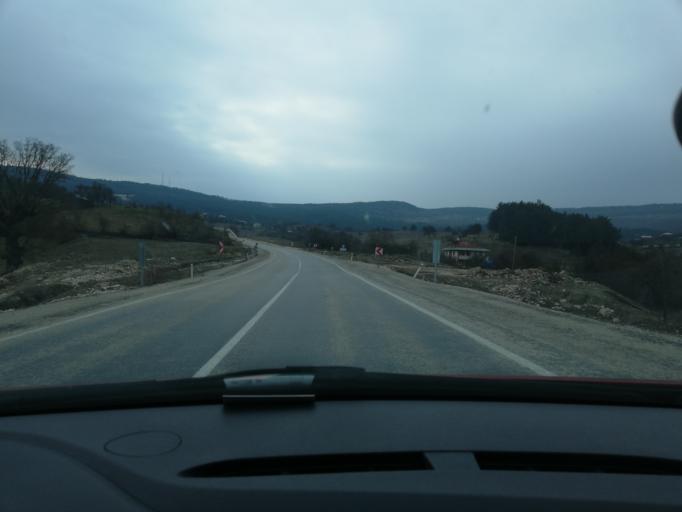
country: TR
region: Kastamonu
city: Pinarbasi
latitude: 41.5873
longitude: 33.0907
